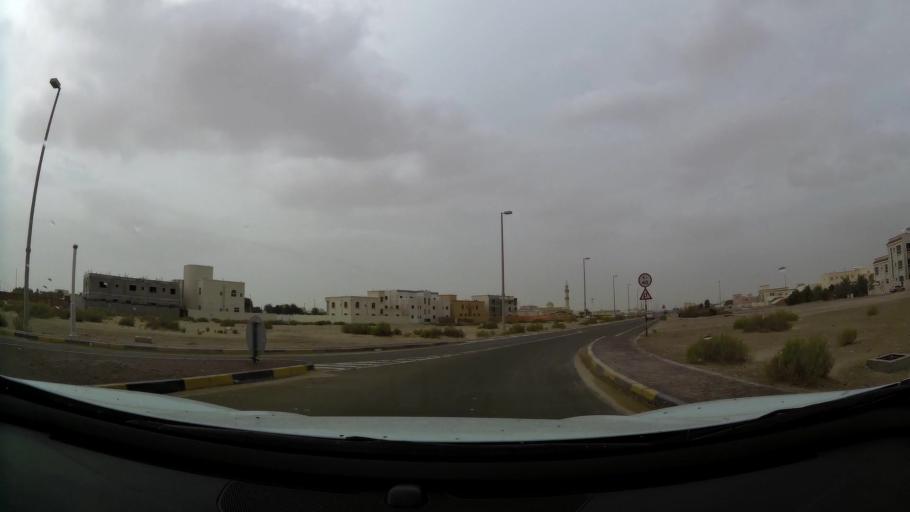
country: AE
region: Abu Dhabi
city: Abu Dhabi
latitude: 24.3573
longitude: 54.6639
